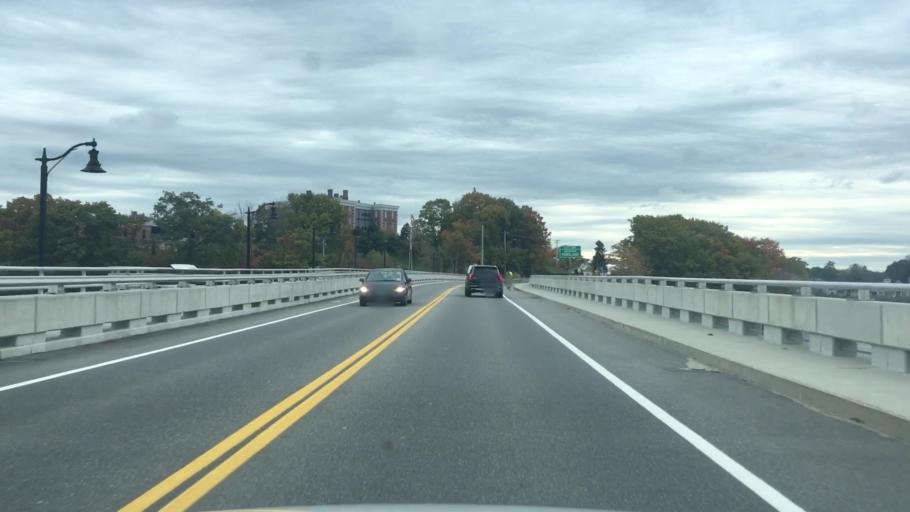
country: US
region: Maine
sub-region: Cumberland County
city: Portland
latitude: 43.6909
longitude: -70.2454
